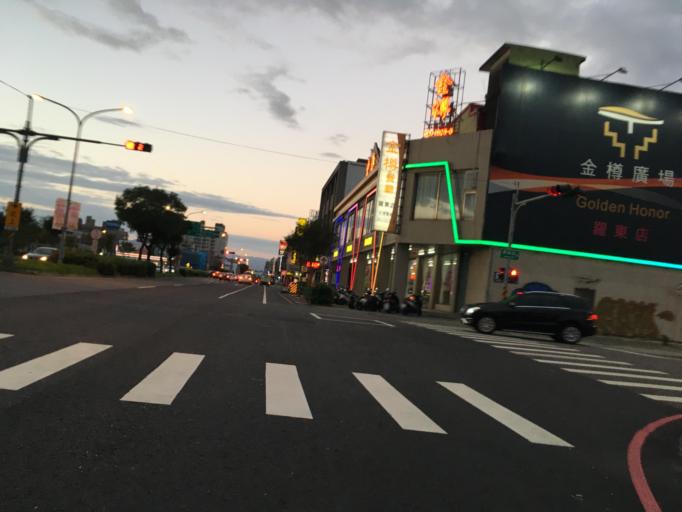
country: TW
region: Taiwan
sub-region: Yilan
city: Yilan
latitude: 24.6765
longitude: 121.7778
